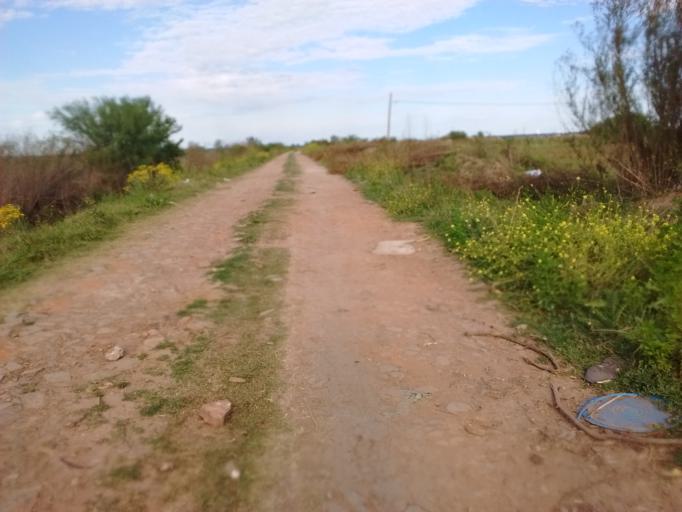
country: AR
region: Santa Fe
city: Funes
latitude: -32.8863
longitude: -60.7959
